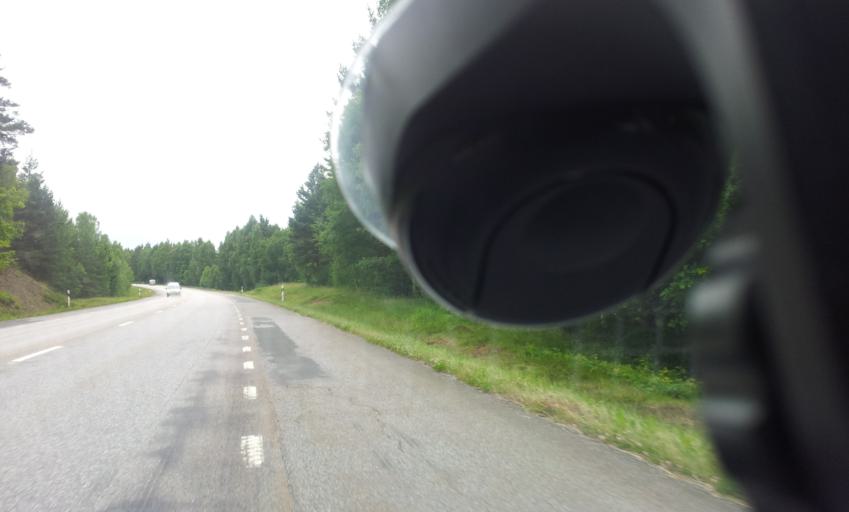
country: SE
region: Kalmar
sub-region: Vasterviks Kommun
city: Ankarsrum
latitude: 57.6941
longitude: 16.4402
